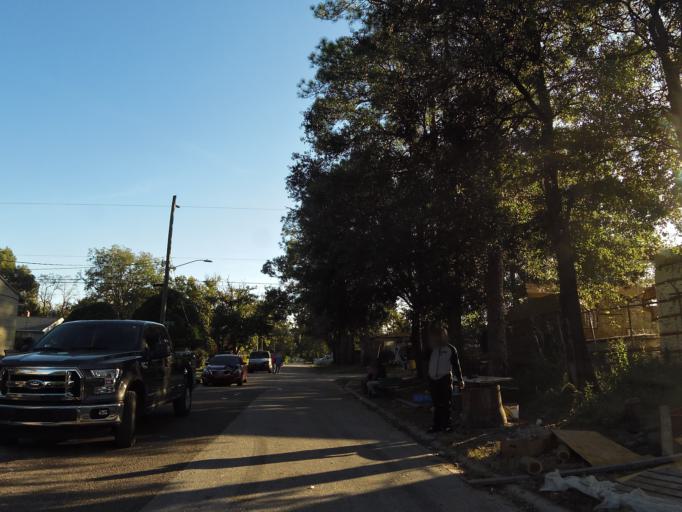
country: US
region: Florida
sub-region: Duval County
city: Jacksonville
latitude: 30.3549
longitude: -81.6943
